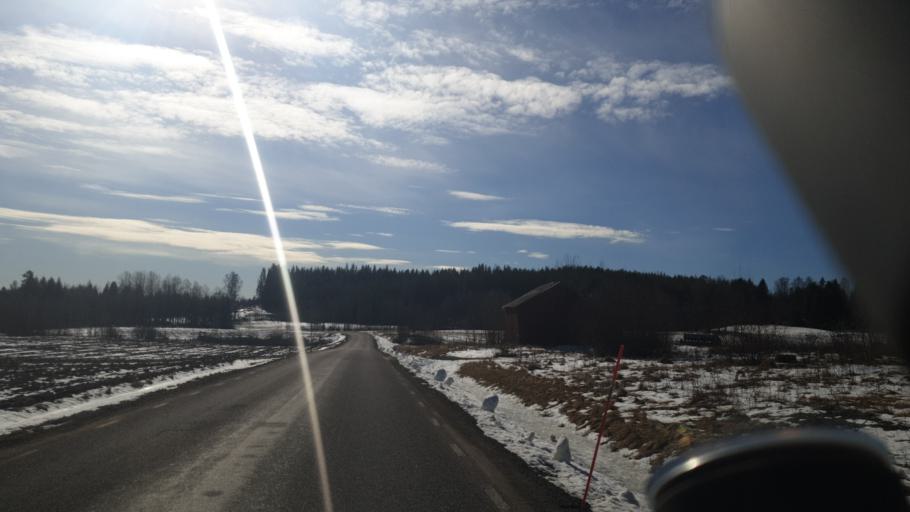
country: SE
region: Vaermland
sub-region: Grums Kommun
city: Slottsbron
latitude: 59.4631
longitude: 12.8764
